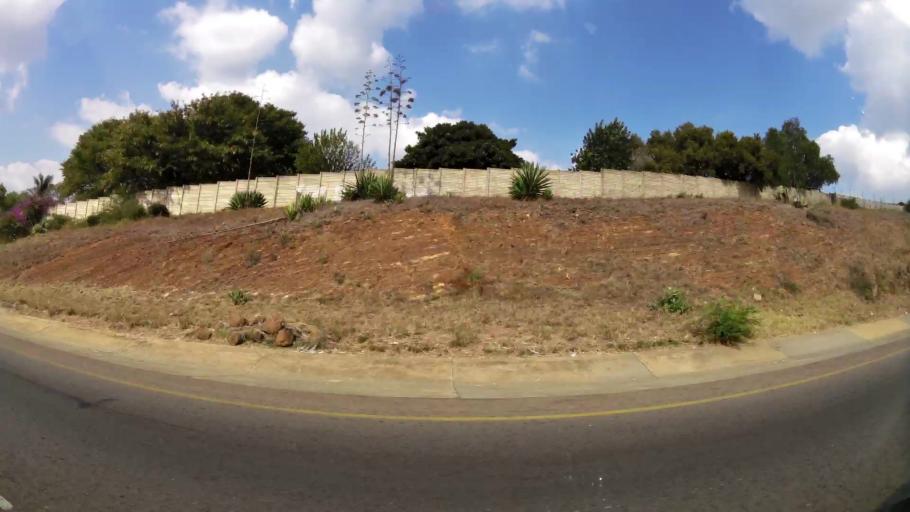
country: ZA
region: Gauteng
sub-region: City of Tshwane Metropolitan Municipality
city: Centurion
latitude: -25.8116
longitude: 28.2819
